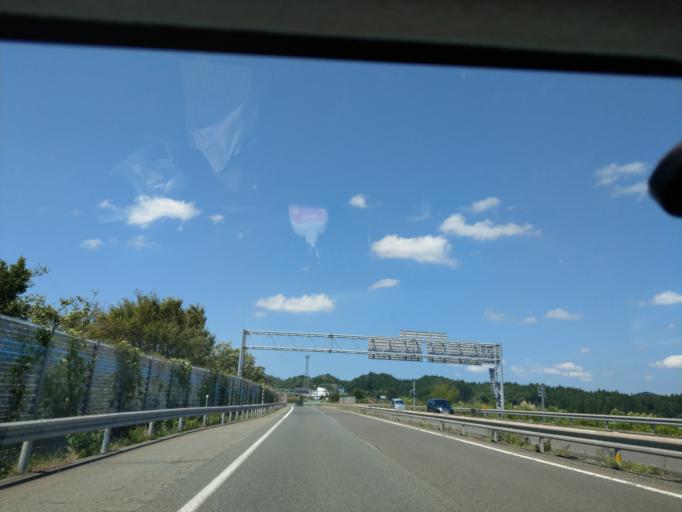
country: JP
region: Akita
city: Akita
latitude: 39.6485
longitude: 140.2070
